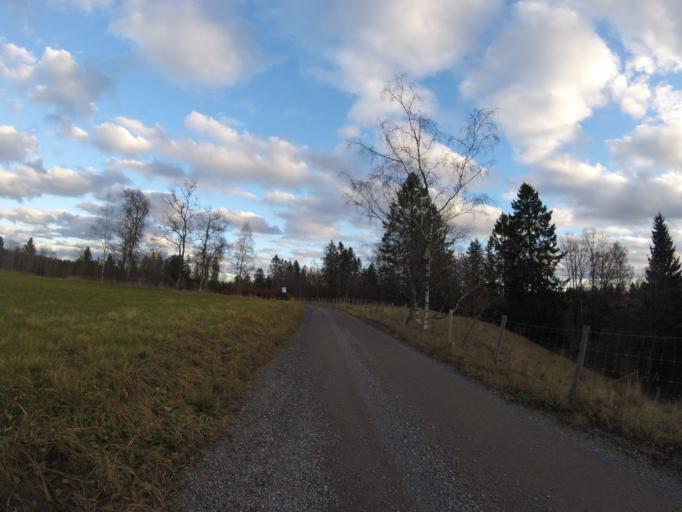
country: NO
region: Akershus
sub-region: Skedsmo
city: Leirsund
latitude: 60.0004
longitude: 11.0540
